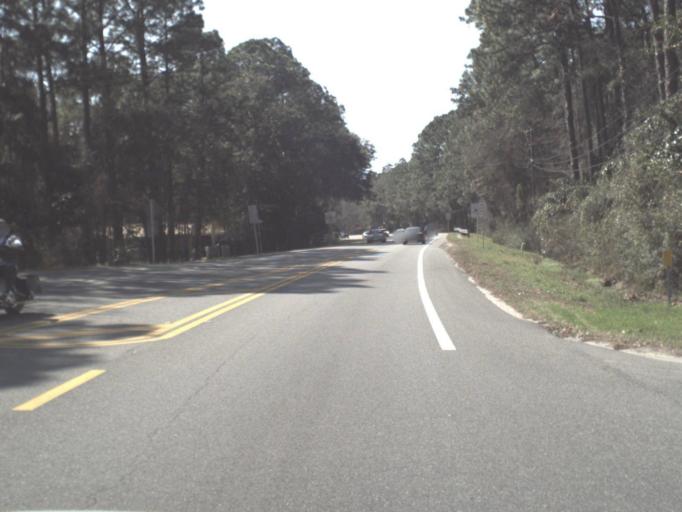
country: US
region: Florida
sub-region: Bay County
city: Lynn Haven
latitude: 30.2288
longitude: -85.6580
